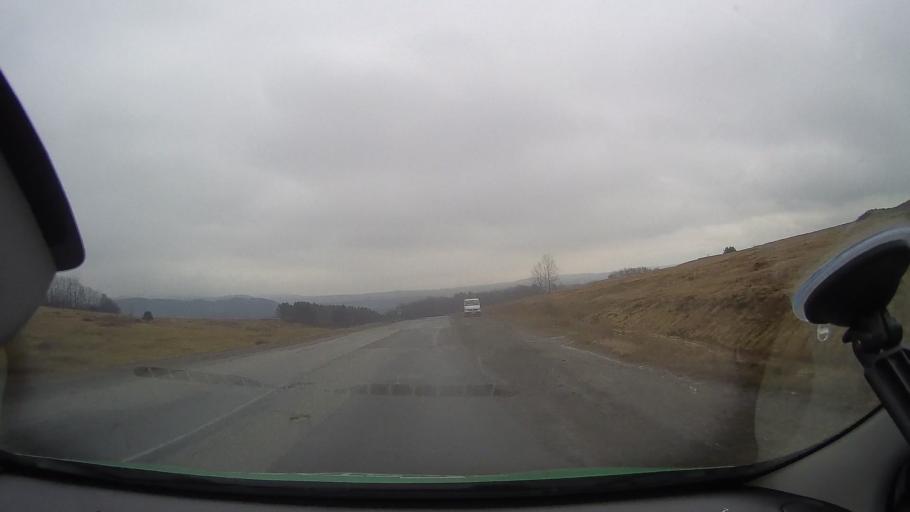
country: RO
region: Arad
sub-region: Comuna Halmagiu
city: Halmagiu
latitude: 46.2820
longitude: 22.5840
